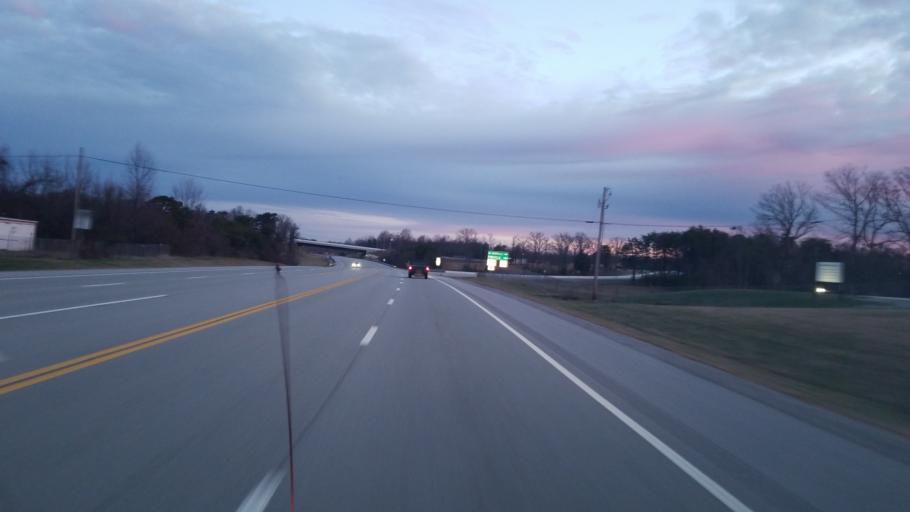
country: US
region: Tennessee
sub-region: Van Buren County
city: Spencer
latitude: 35.7387
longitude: -85.4587
